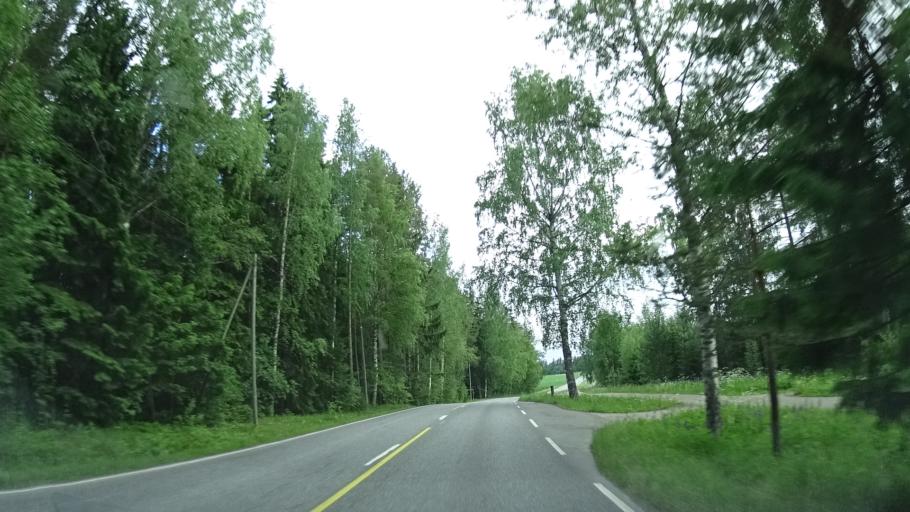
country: FI
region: Paijanne Tavastia
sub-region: Lahti
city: Asikkala
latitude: 61.2537
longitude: 25.5124
